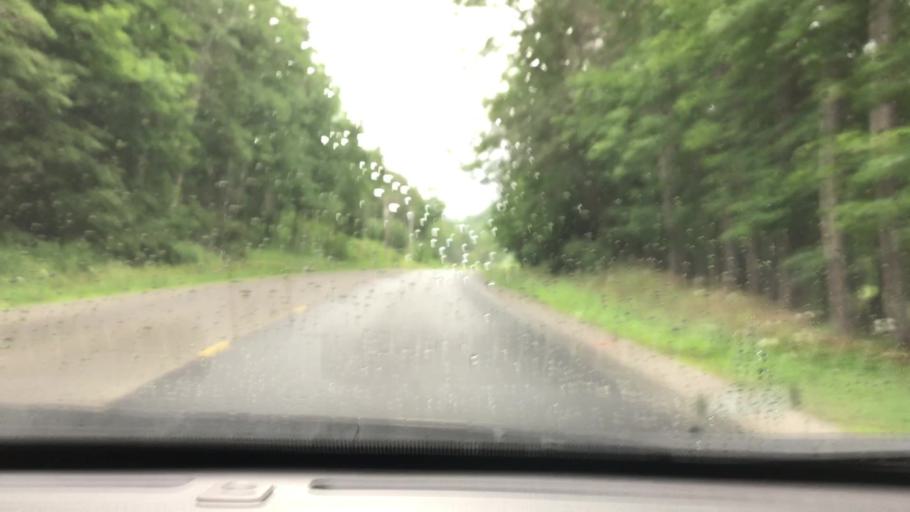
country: US
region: New York
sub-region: Cattaraugus County
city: Salamanca
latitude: 42.2910
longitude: -78.6629
